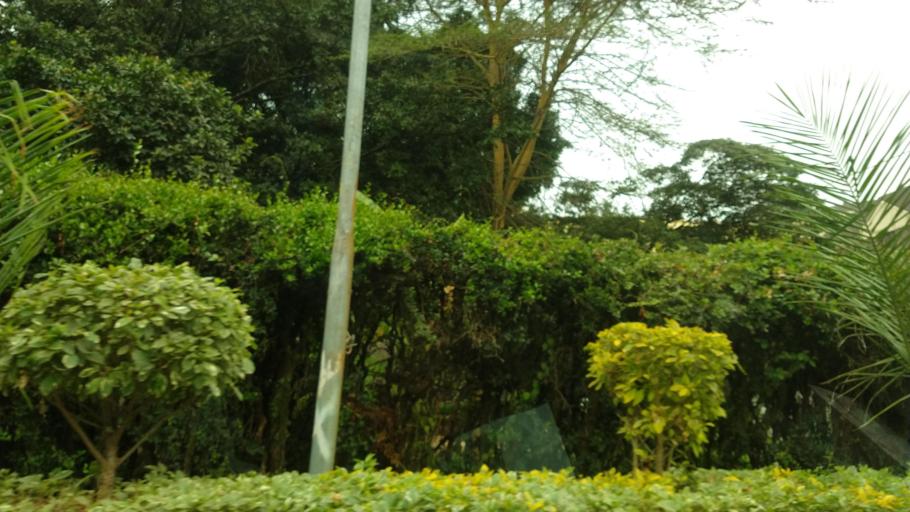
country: KE
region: Nairobi Area
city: Nairobi
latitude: -1.2909
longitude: 36.7817
